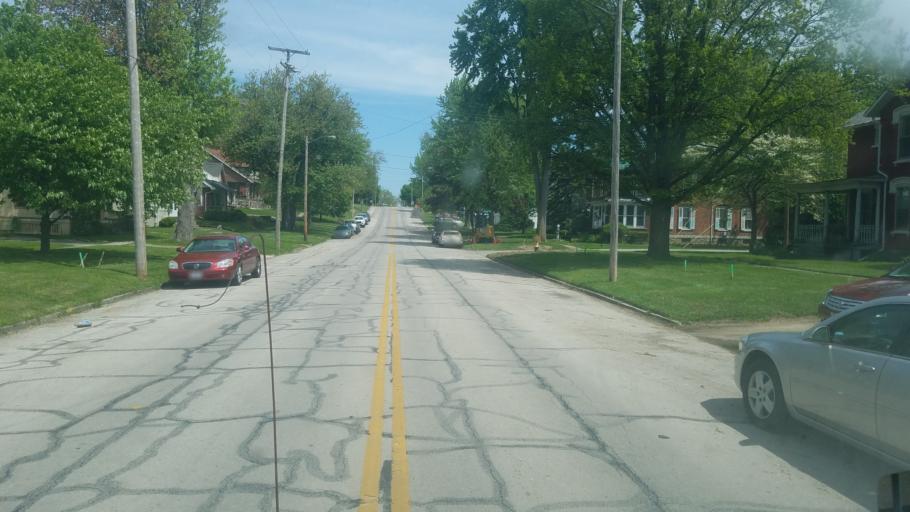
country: US
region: Ohio
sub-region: Sandusky County
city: Fremont
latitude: 41.3402
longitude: -83.1174
